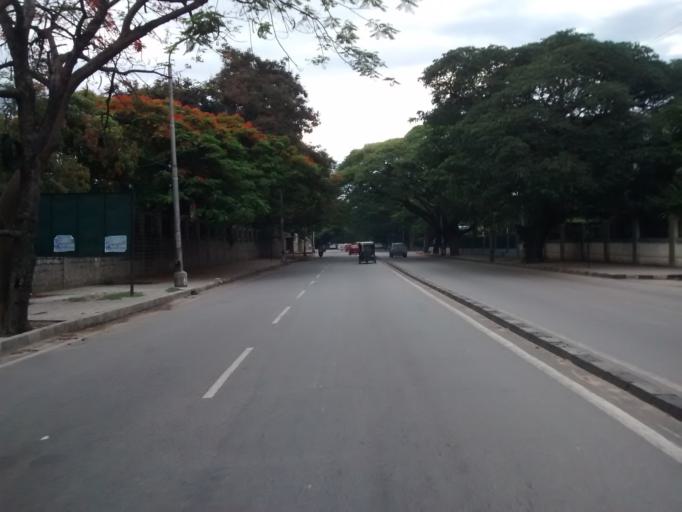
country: IN
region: Karnataka
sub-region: Bangalore Urban
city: Bangalore
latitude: 12.9580
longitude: 77.6698
